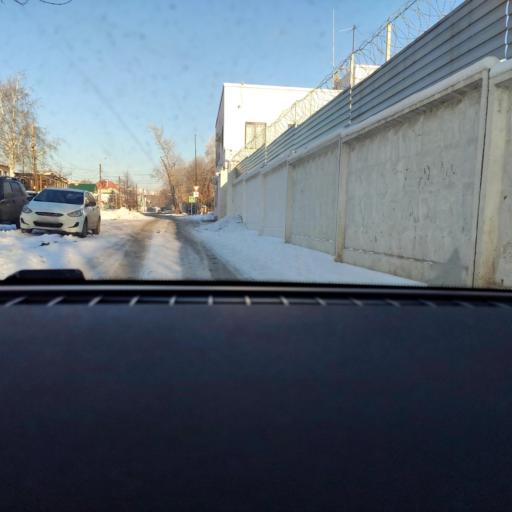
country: RU
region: Samara
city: Samara
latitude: 53.1799
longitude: 50.1336
